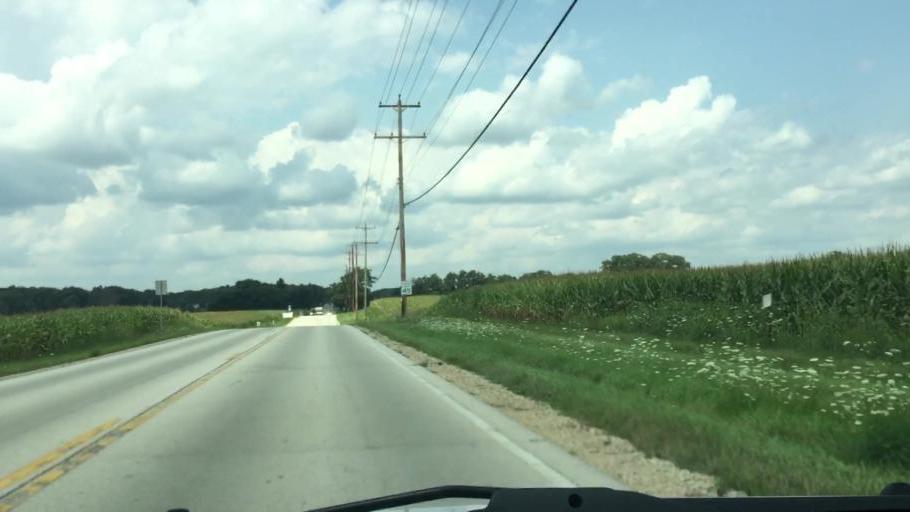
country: US
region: Wisconsin
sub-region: Waukesha County
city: North Prairie
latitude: 42.9397
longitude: -88.4056
